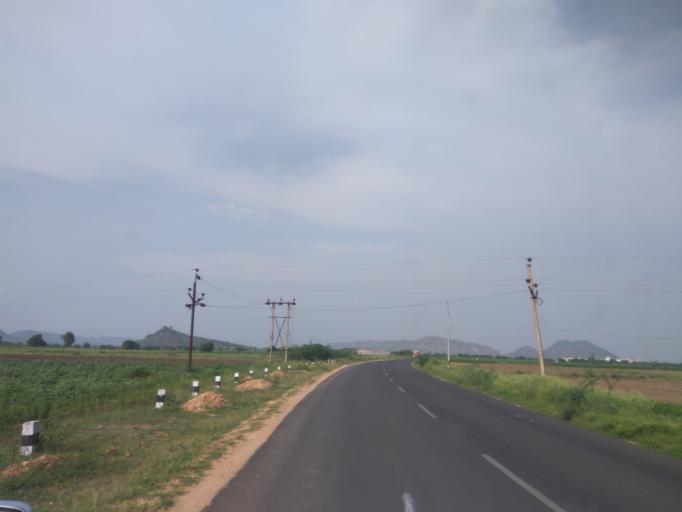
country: IN
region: Andhra Pradesh
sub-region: Prakasam
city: Markapur
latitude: 15.7815
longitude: 79.2466
